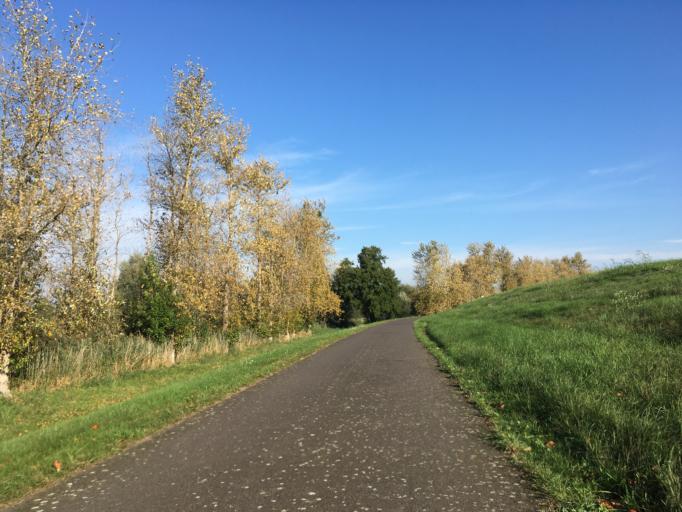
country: DE
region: Brandenburg
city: Reitwein
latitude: 52.5477
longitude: 14.6087
